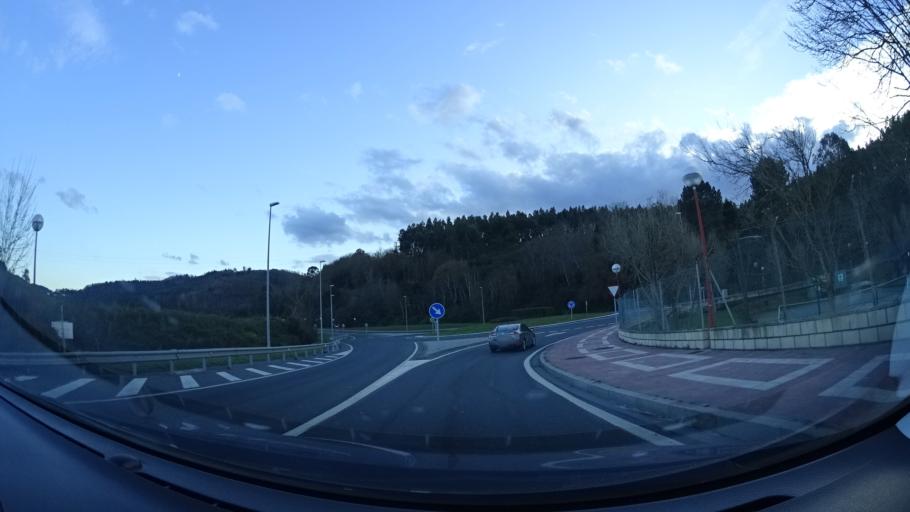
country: ES
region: Basque Country
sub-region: Bizkaia
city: Plentzia
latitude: 43.3972
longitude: -2.9440
